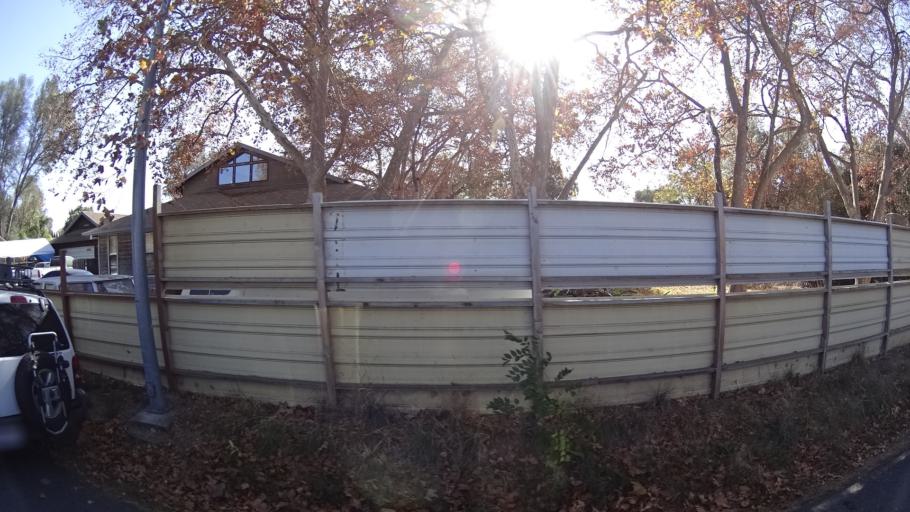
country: US
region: California
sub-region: Sacramento County
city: Citrus Heights
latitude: 38.7061
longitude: -121.2785
